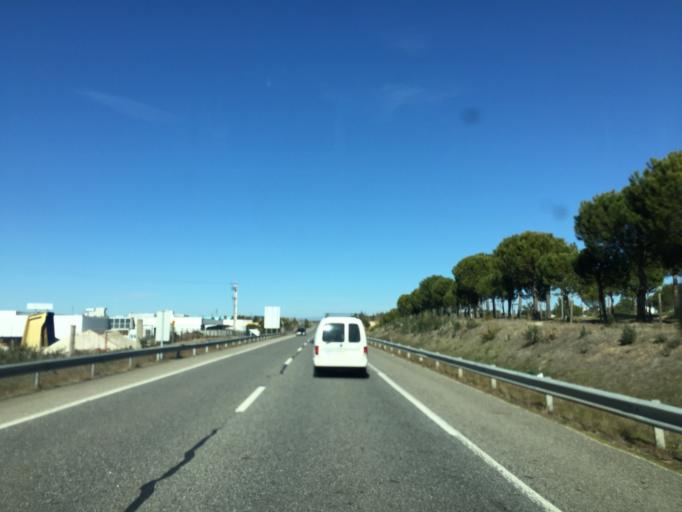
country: PT
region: Castelo Branco
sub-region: Castelo Branco
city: Castelo Branco
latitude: 39.8139
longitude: -7.5172
